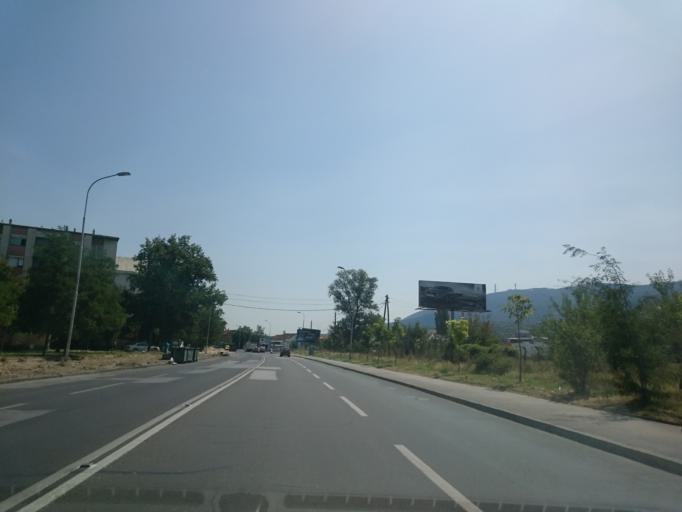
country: MK
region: Saraj
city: Saraj
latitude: 42.0066
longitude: 21.3425
